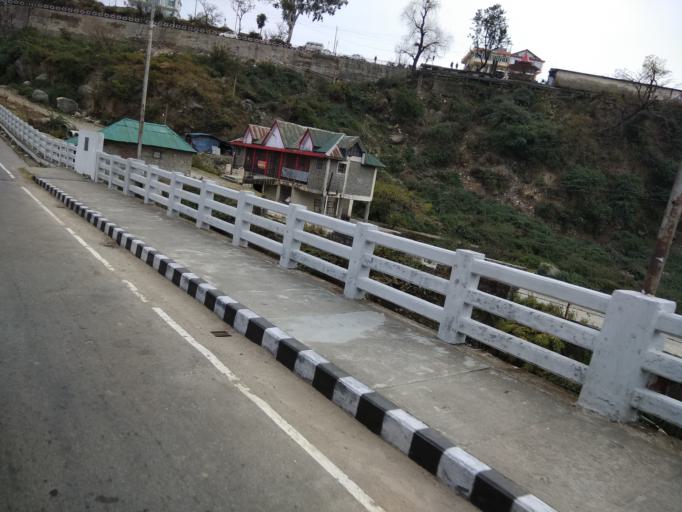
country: IN
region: Himachal Pradesh
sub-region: Kangra
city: Dharmsala
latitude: 32.1482
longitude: 76.4211
